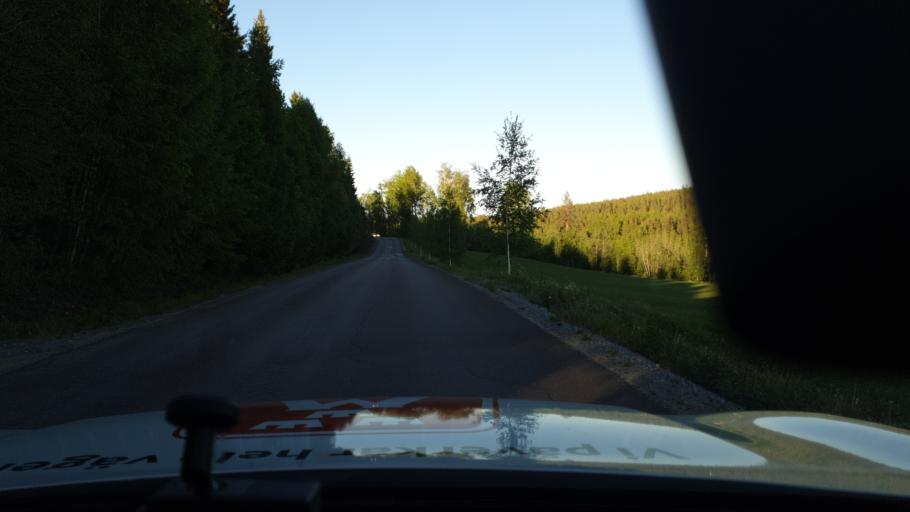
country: SE
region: Vaesterbotten
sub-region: Umea Kommun
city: Roback
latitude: 64.0102
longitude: 20.1623
